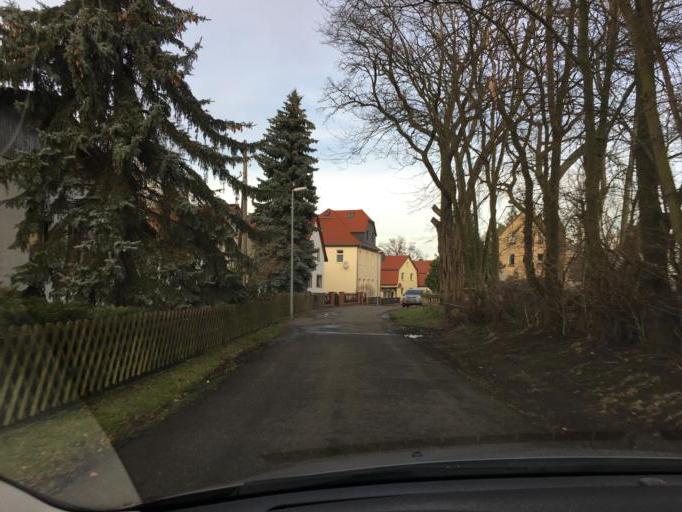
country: DE
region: Thuringia
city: Fockendorf
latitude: 51.0693
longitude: 12.4645
